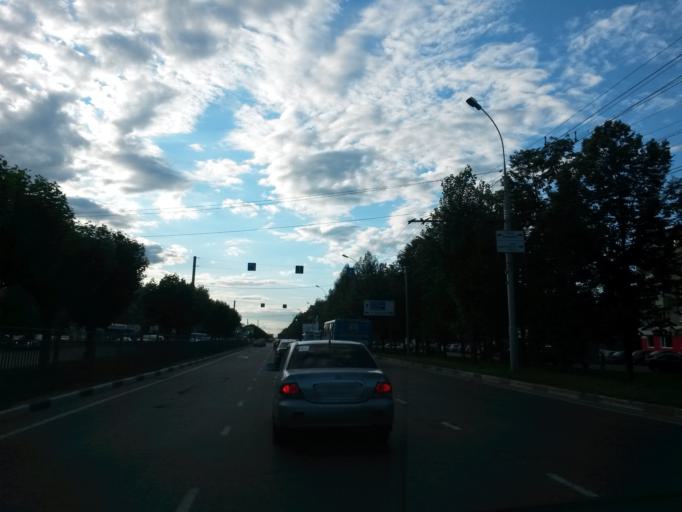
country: RU
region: Jaroslavl
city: Yaroslavl
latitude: 57.6799
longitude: 39.7951
